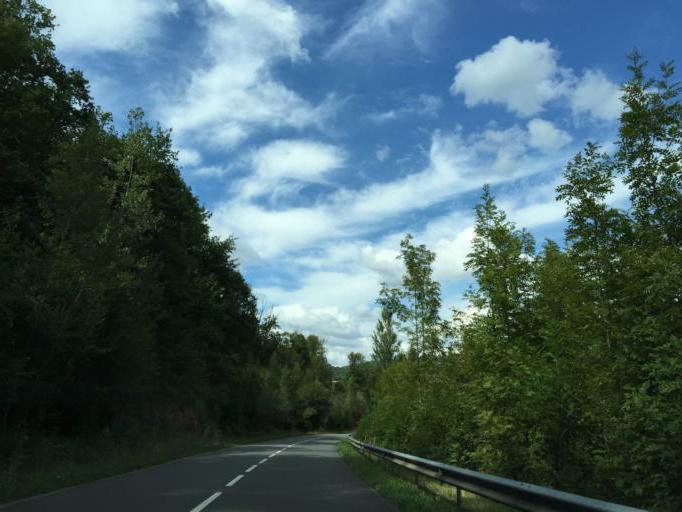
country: FR
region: Midi-Pyrenees
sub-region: Departement de l'Aveyron
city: Marcillac-Vallon
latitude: 44.4854
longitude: 2.4500
